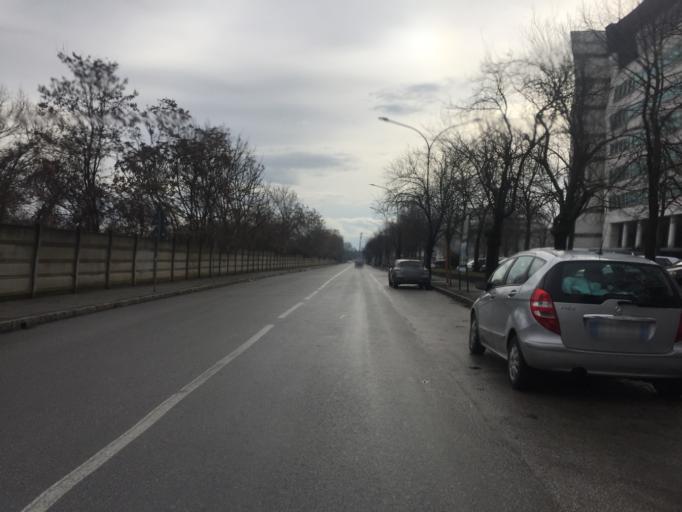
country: IT
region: Emilia-Romagna
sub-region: Provincia di Bologna
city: Bologna
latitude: 44.5095
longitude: 11.3045
